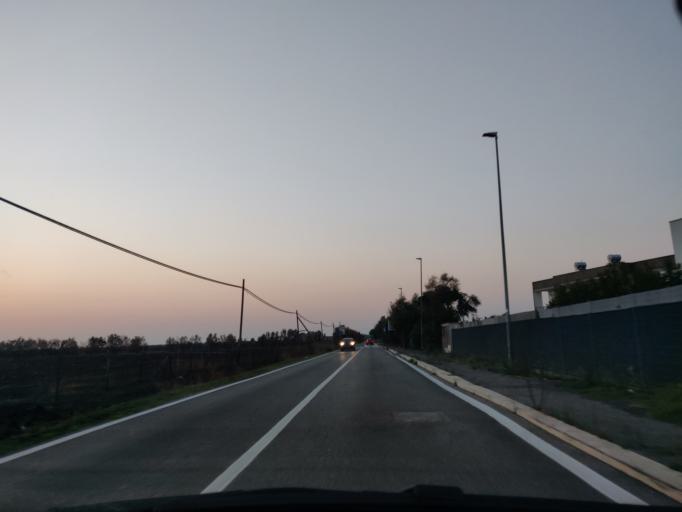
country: IT
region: Latium
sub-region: Citta metropolitana di Roma Capitale
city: Npp 23 (Parco Leonardo)
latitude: 41.8150
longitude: 12.2998
